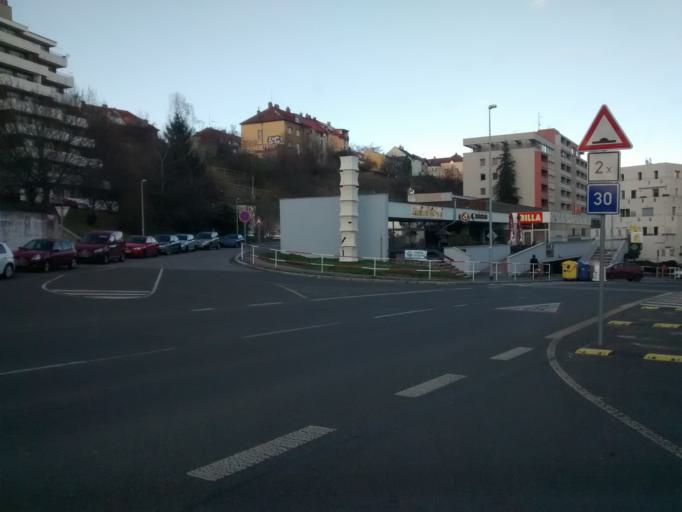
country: CZ
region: Praha
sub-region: Praha 1
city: Mala Strana
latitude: 50.0874
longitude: 14.3652
